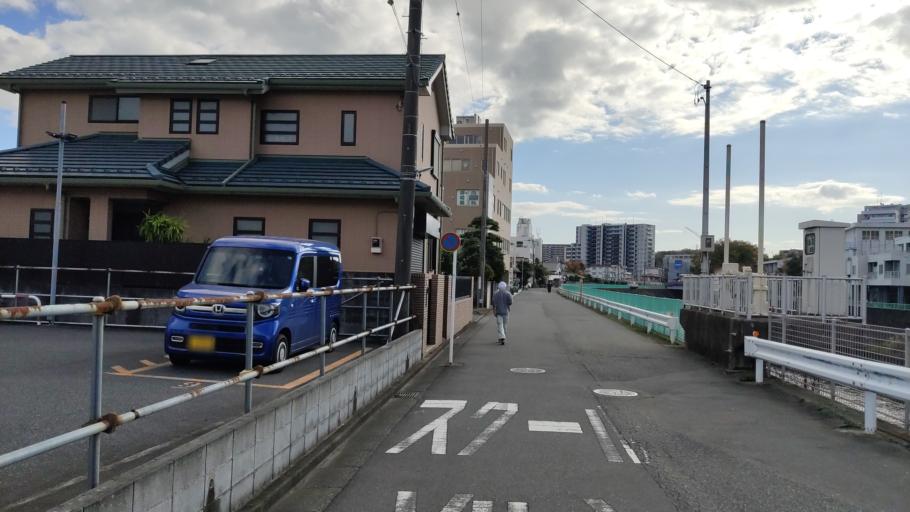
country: JP
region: Kanagawa
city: Fujisawa
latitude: 35.3402
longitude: 139.4940
